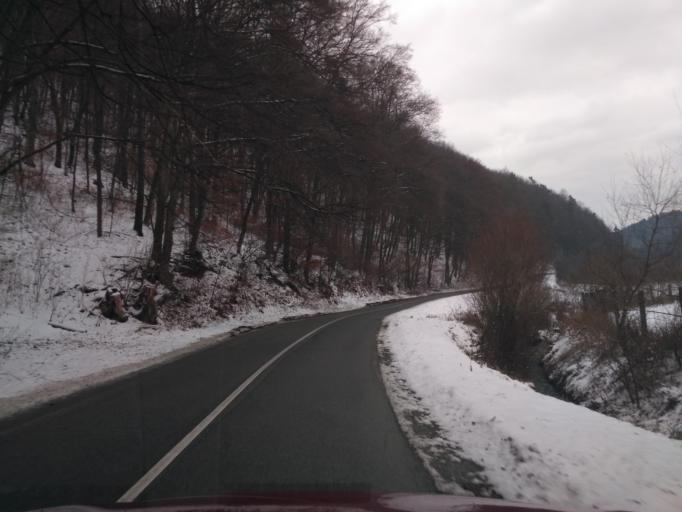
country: SK
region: Presovsky
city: Sabinov
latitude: 48.9643
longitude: 21.0970
